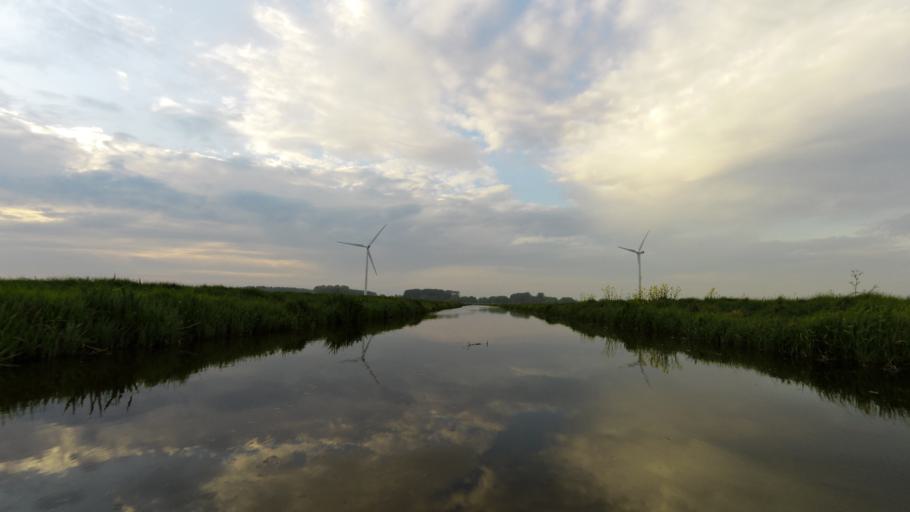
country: NL
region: South Holland
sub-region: Gemeente Alphen aan den Rijn
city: Alphen aan den Rijn
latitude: 52.1187
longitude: 4.6102
